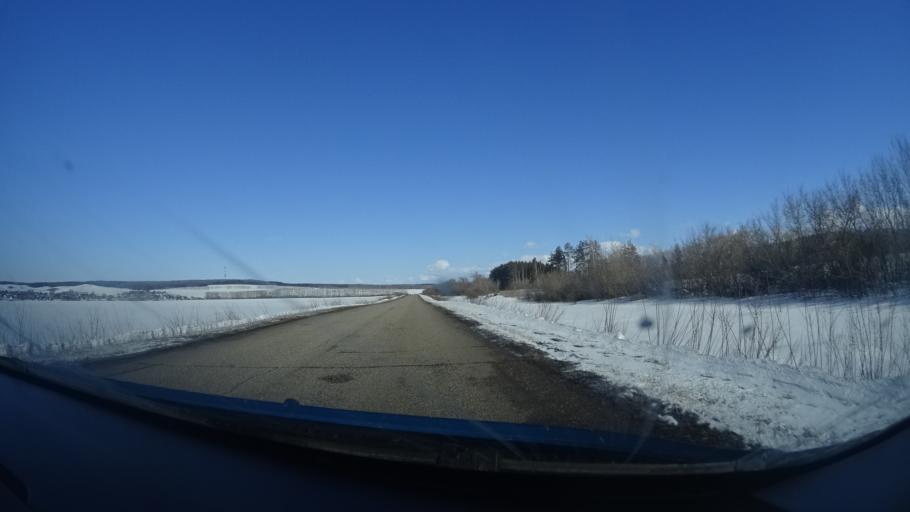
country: RU
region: Bashkortostan
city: Chishmy
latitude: 54.5937
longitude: 55.3315
